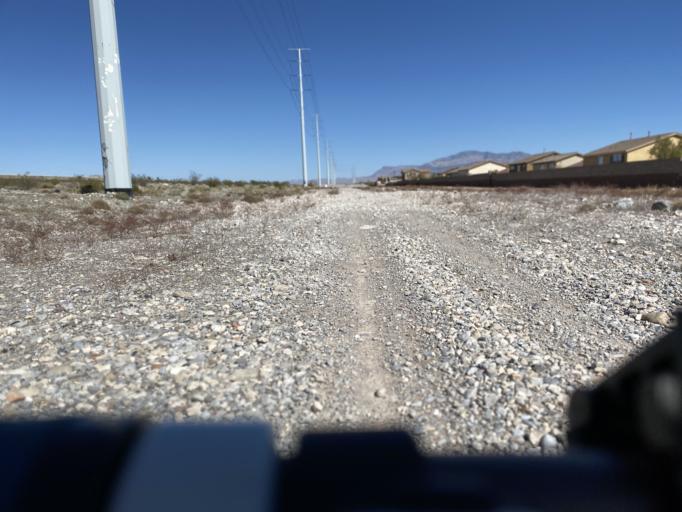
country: US
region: Nevada
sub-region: Clark County
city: Summerlin South
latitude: 36.2968
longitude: -115.3335
